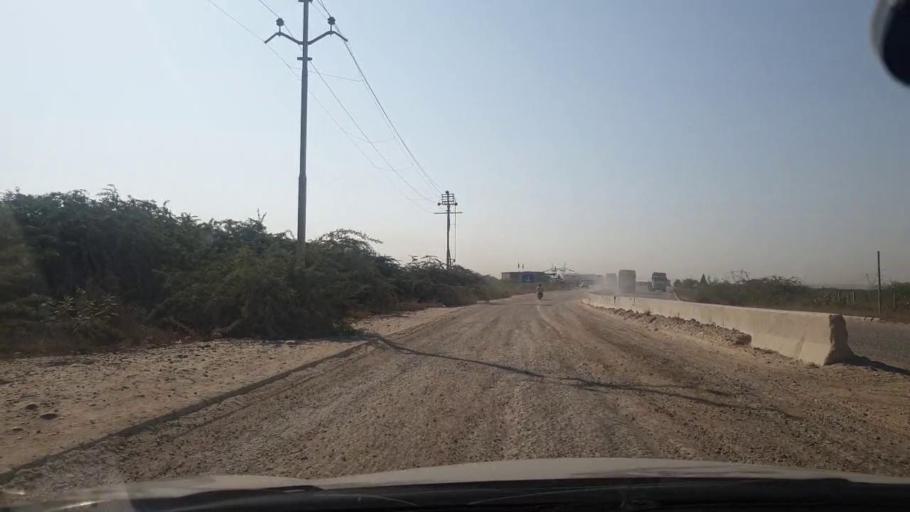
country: PK
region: Sindh
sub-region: Karachi District
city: Karachi
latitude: 25.0766
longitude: 67.0139
